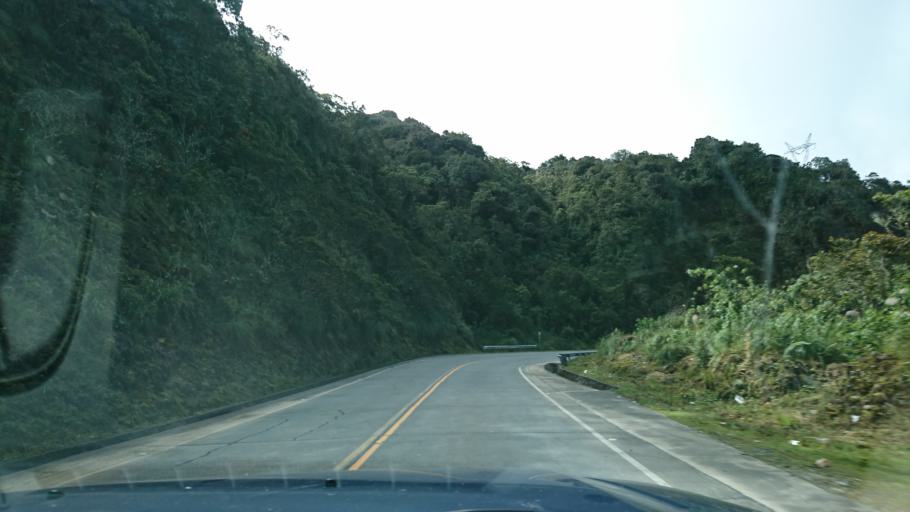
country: BO
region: La Paz
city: Coroico
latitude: -16.2861
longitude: -67.8455
